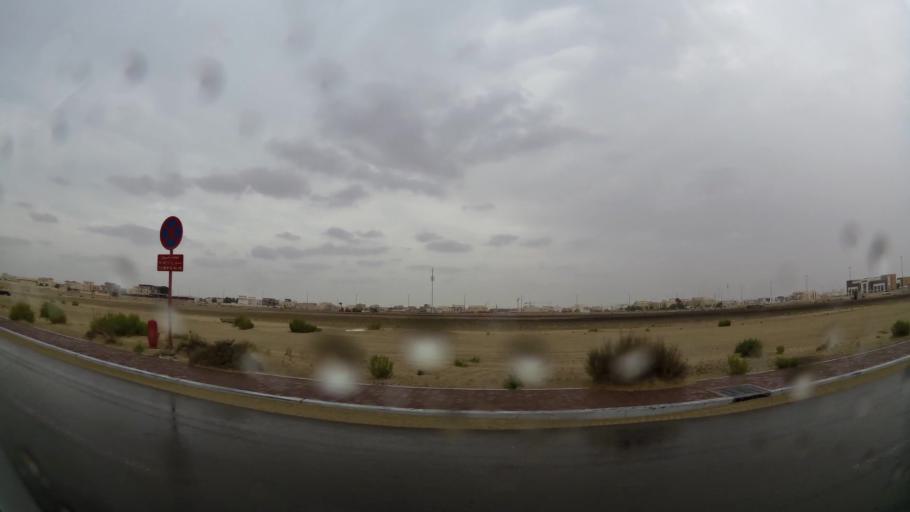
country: AE
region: Abu Dhabi
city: Abu Dhabi
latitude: 24.3635
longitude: 54.6315
